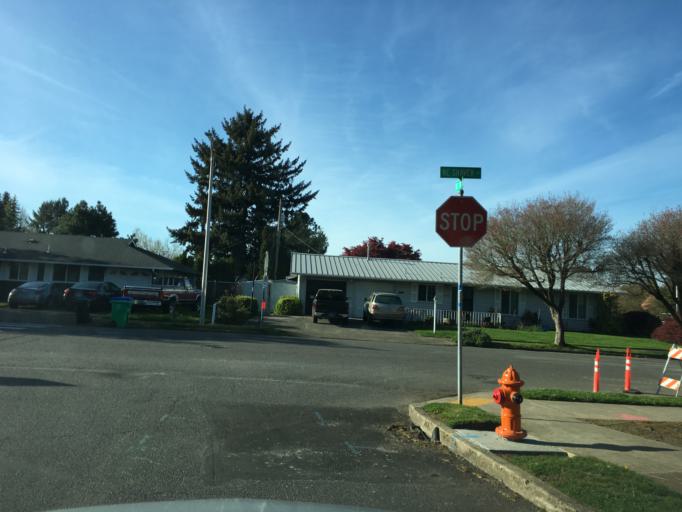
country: US
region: Oregon
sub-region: Multnomah County
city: Lents
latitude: 45.5523
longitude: -122.5252
